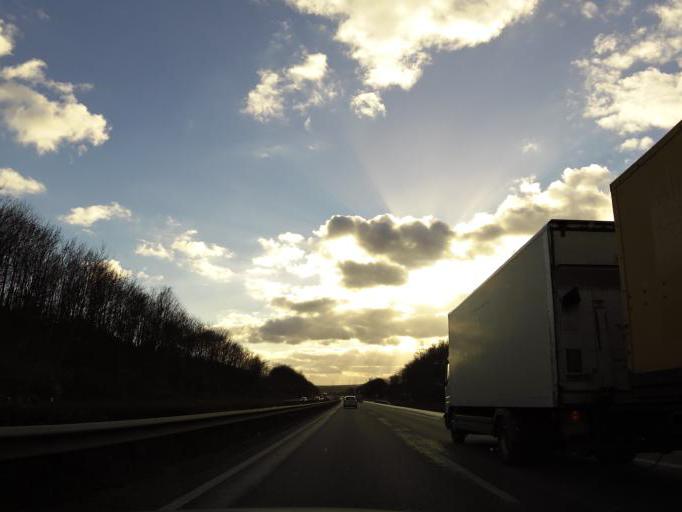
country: DE
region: Rheinland-Pfalz
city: Ober-Olm
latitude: 49.9274
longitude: 8.1985
